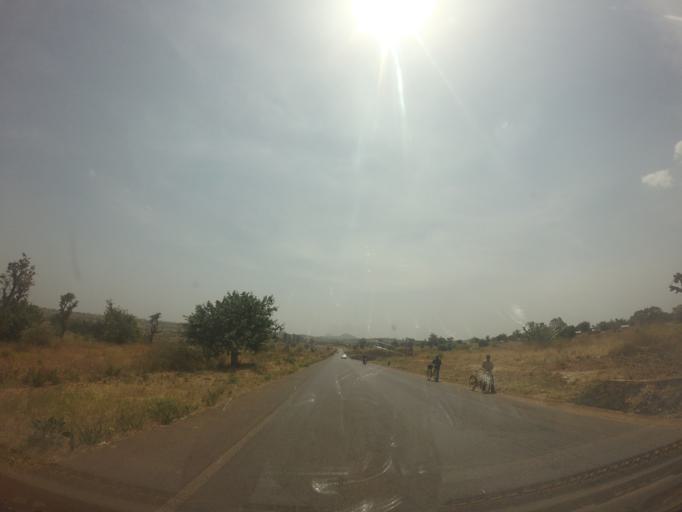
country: UG
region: Northern Region
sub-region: Arua District
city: Arua
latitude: 2.9483
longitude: 30.9397
